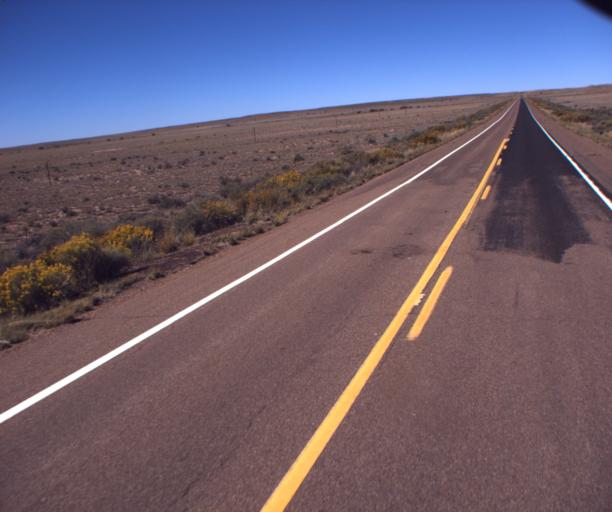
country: US
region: Arizona
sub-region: Navajo County
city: Snowflake
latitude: 34.7549
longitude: -109.8060
